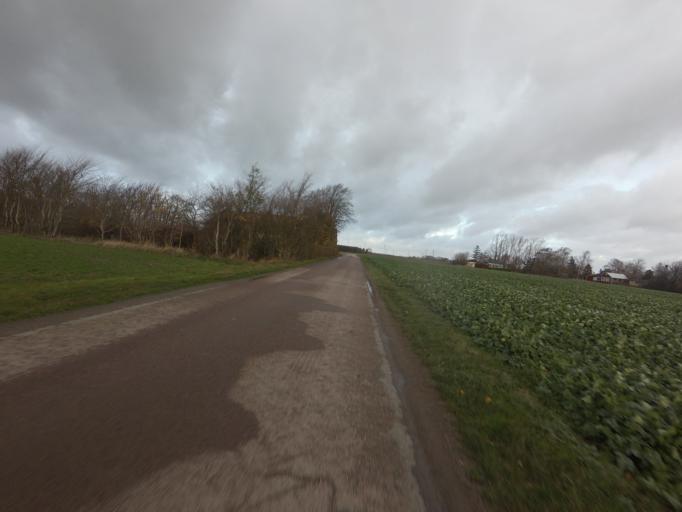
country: SE
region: Skane
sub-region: Helsingborg
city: Odakra
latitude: 56.1380
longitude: 12.7648
